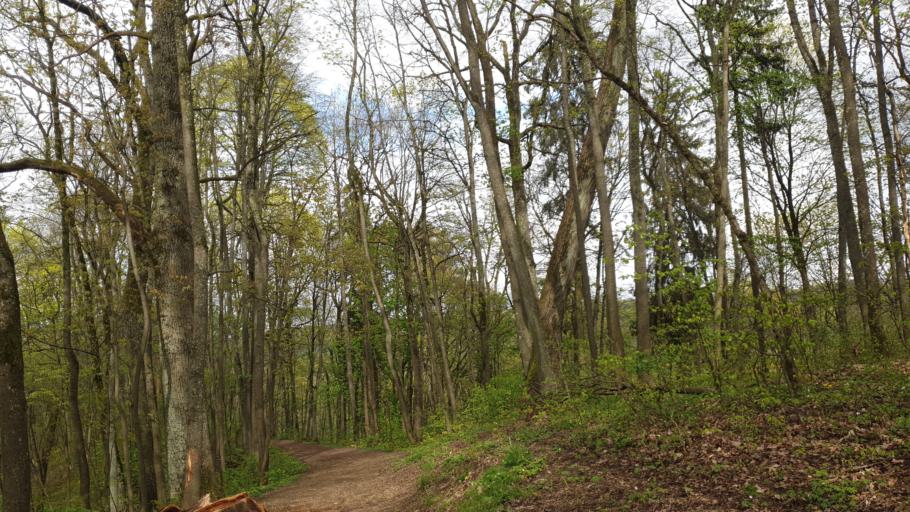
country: LT
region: Kauno apskritis
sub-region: Kauno rajonas
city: Akademija (Kaunas)
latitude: 54.9446
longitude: 23.7848
